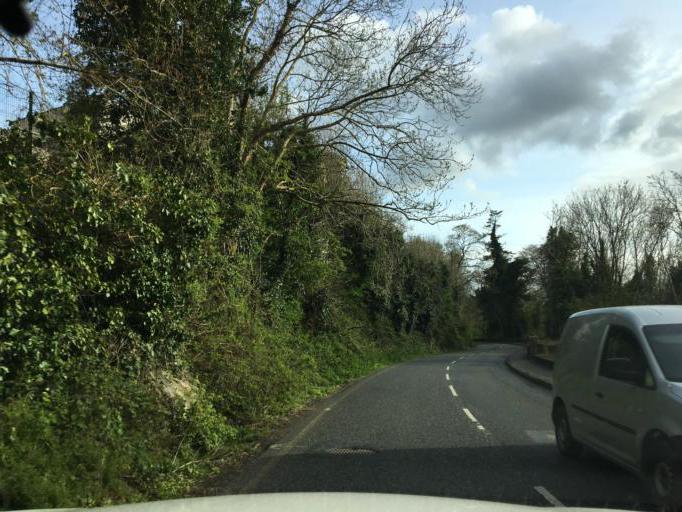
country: IE
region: Leinster
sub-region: Loch Garman
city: New Ross
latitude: 52.4039
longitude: -6.9385
